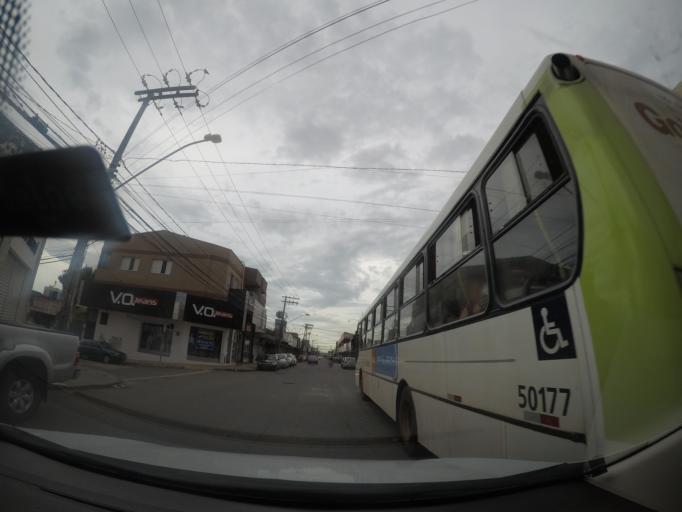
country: BR
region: Goias
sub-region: Goiania
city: Goiania
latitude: -16.6620
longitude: -49.2764
